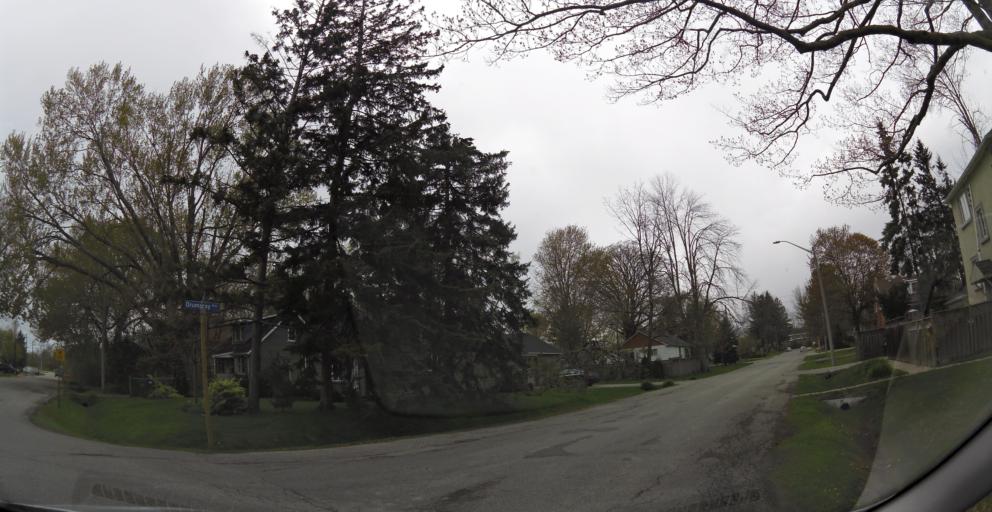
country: CA
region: Ontario
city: Mississauga
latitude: 43.5602
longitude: -79.5835
